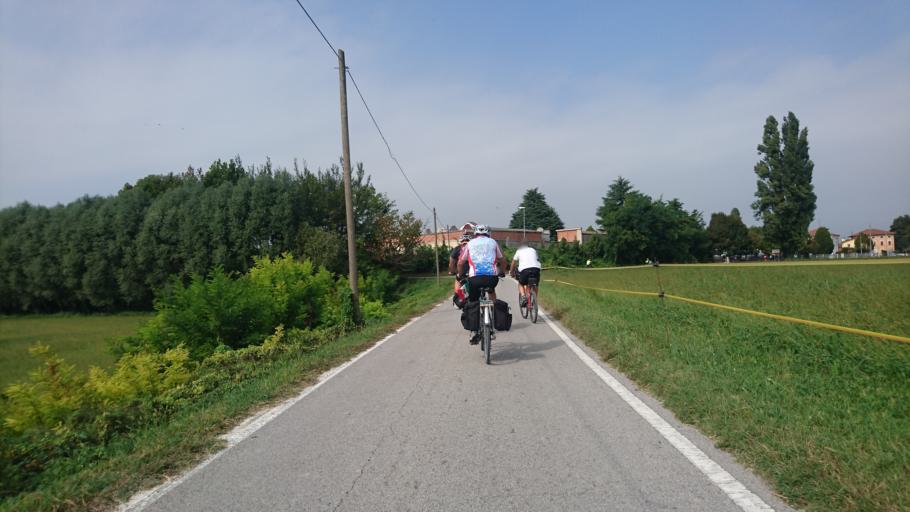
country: IT
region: Veneto
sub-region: Provincia di Padova
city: Grantorto
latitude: 45.5844
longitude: 11.7468
